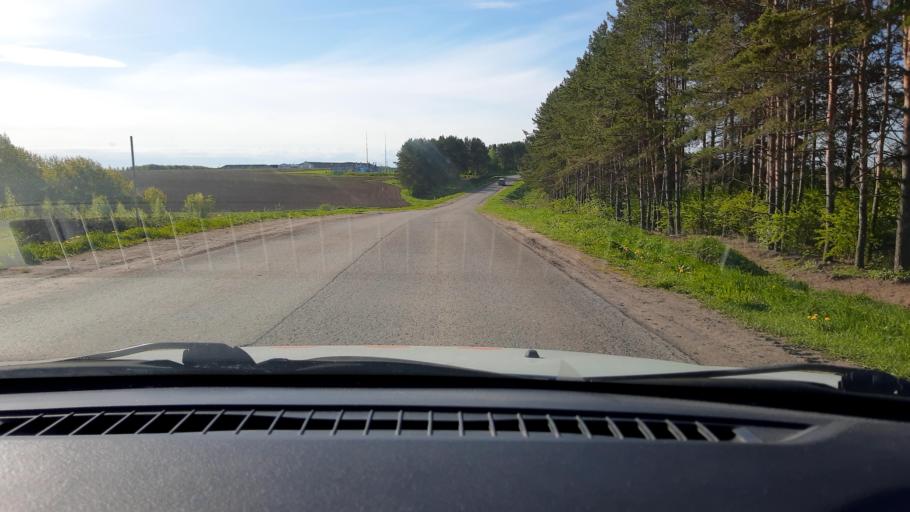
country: RU
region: Nizjnij Novgorod
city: Burevestnik
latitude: 56.1618
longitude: 43.7735
